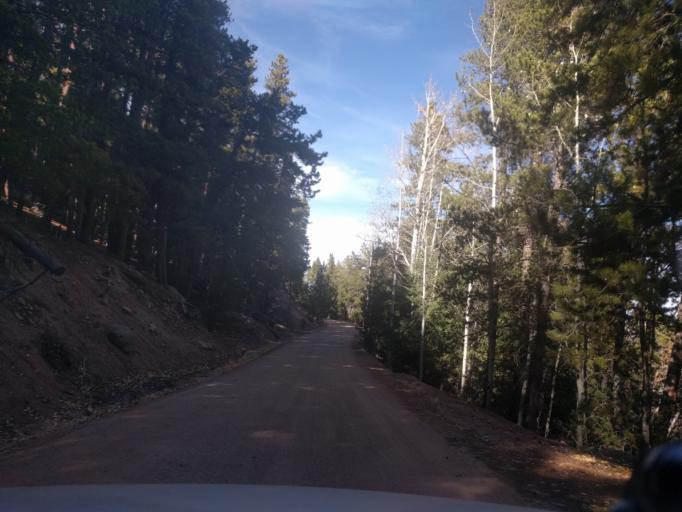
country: US
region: Colorado
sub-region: Douglas County
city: Perry Park
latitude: 39.2024
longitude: -105.0510
